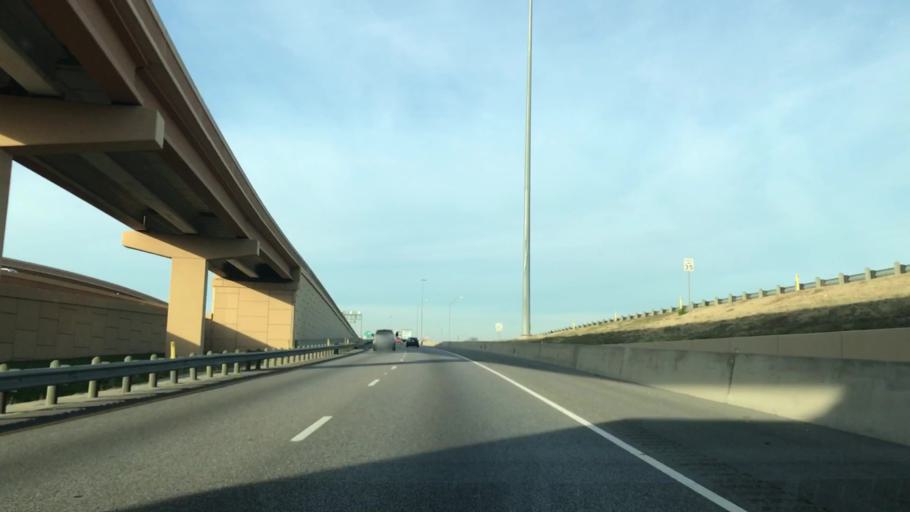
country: US
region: Texas
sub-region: Tarrant County
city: Watauga
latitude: 32.8399
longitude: -97.2807
